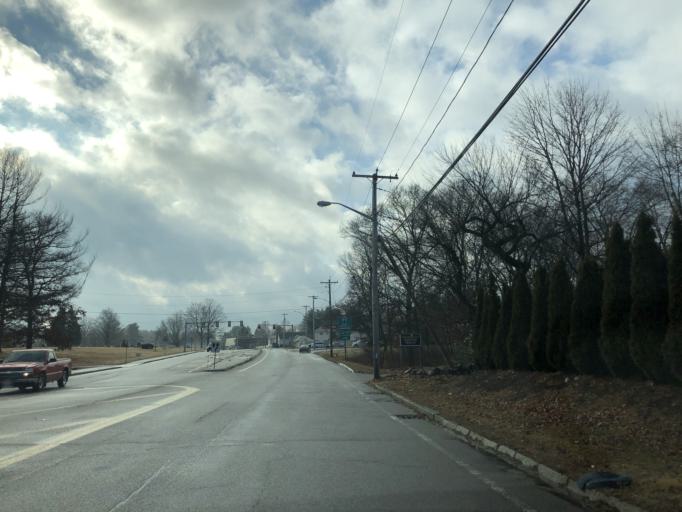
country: US
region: Massachusetts
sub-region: Bristol County
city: Attleboro
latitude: 41.9708
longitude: -71.2915
